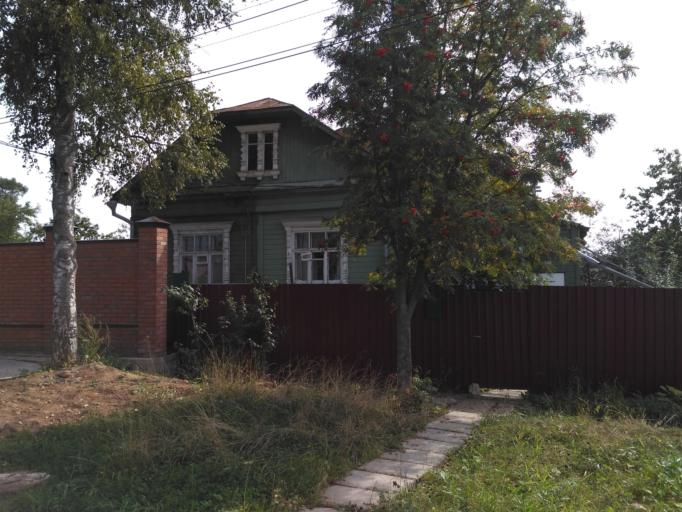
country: RU
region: Moskovskaya
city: Sergiyev Posad
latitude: 56.3064
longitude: 38.1241
